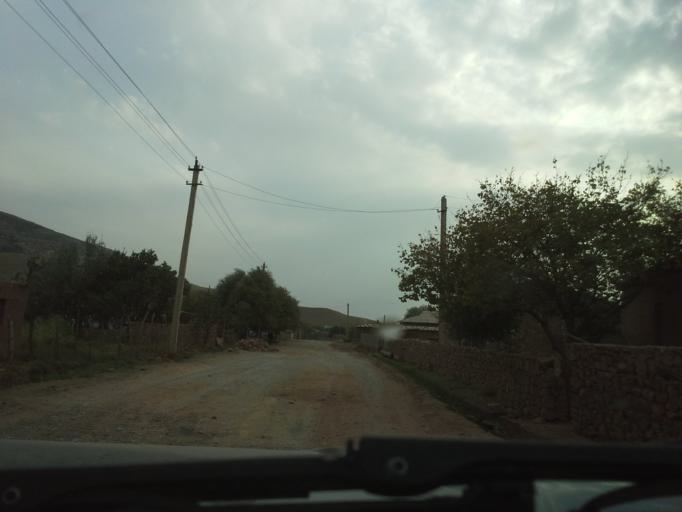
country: UZ
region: Qashqadaryo
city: Qorashina
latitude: 37.9292
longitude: 66.4960
